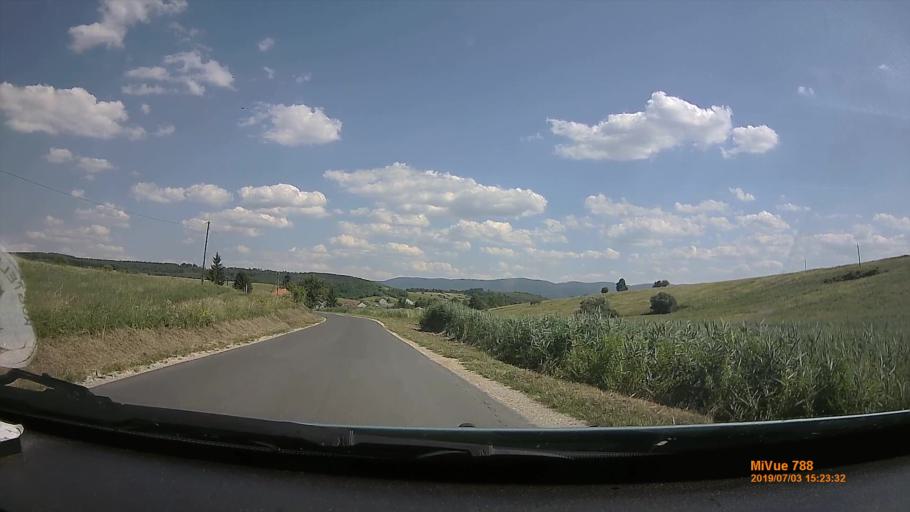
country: HU
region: Borsod-Abauj-Zemplen
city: Farkaslyuk
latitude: 48.1980
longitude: 20.3877
